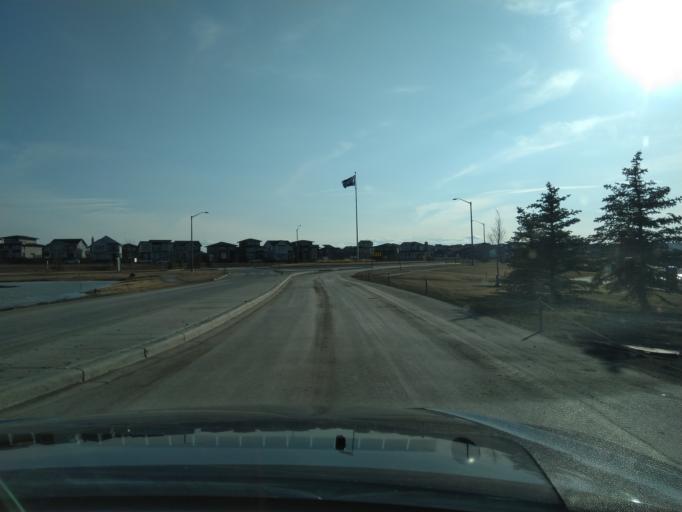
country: CA
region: Alberta
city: Cochrane
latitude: 51.1139
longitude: -114.3918
